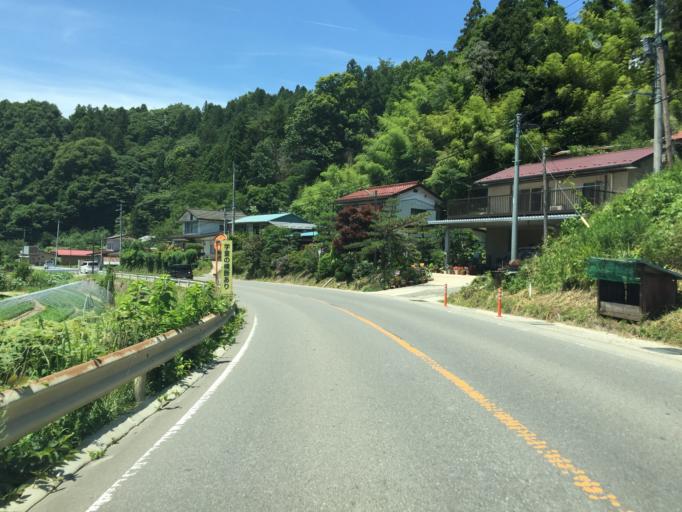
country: JP
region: Fukushima
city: Yanagawamachi-saiwaicho
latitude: 37.7611
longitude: 140.6394
